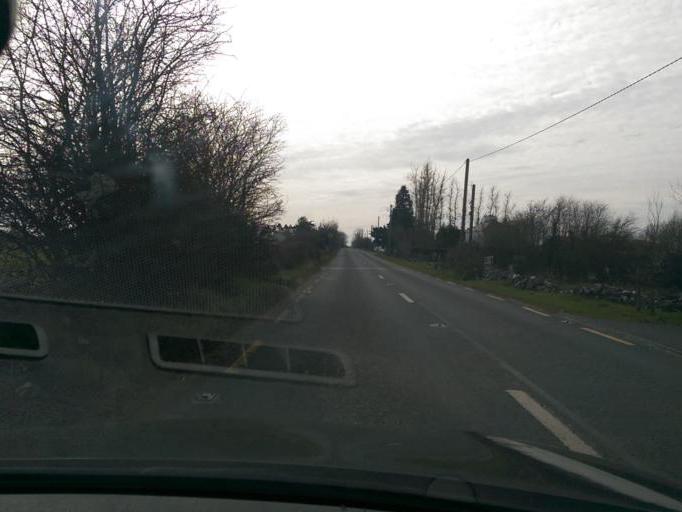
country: IE
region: Connaught
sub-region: County Galway
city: Claregalway
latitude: 53.3880
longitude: -8.8464
